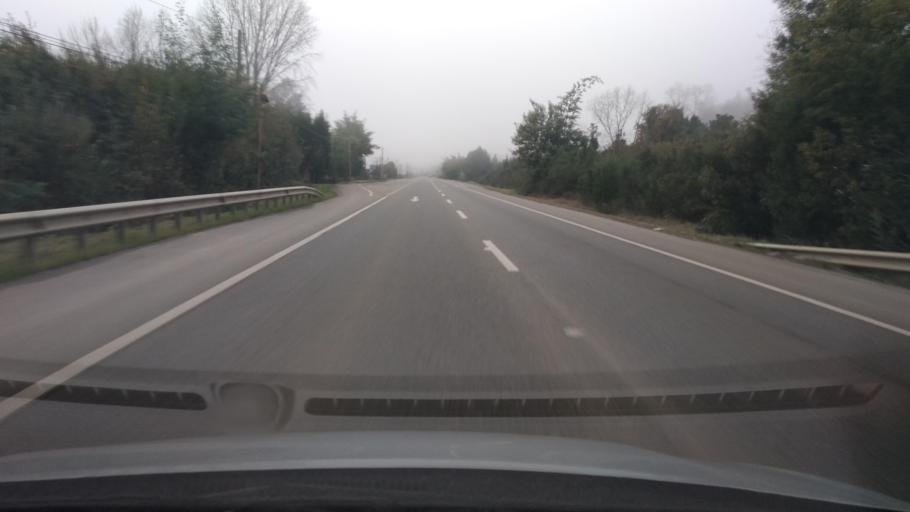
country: CL
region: Los Lagos
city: Las Animas
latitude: -39.7464
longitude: -73.2280
